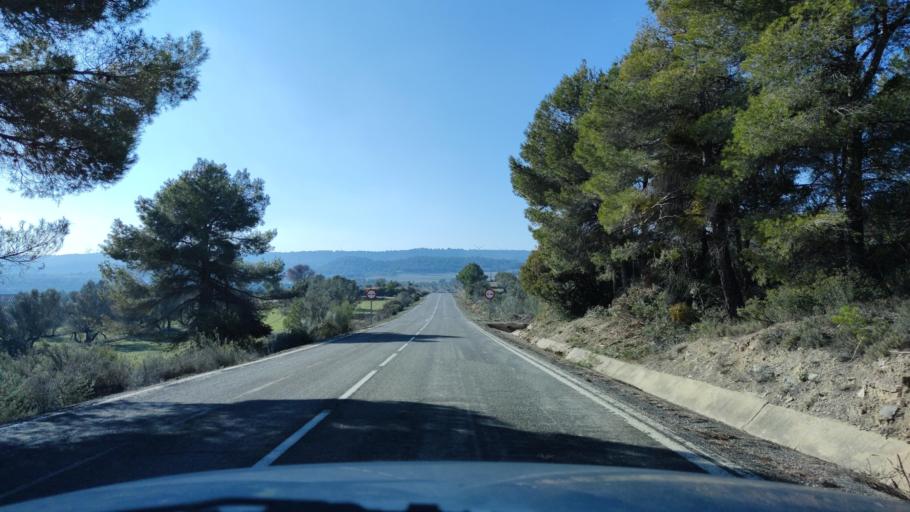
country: ES
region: Catalonia
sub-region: Provincia de Lleida
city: Maials
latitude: 41.3353
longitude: 0.4524
